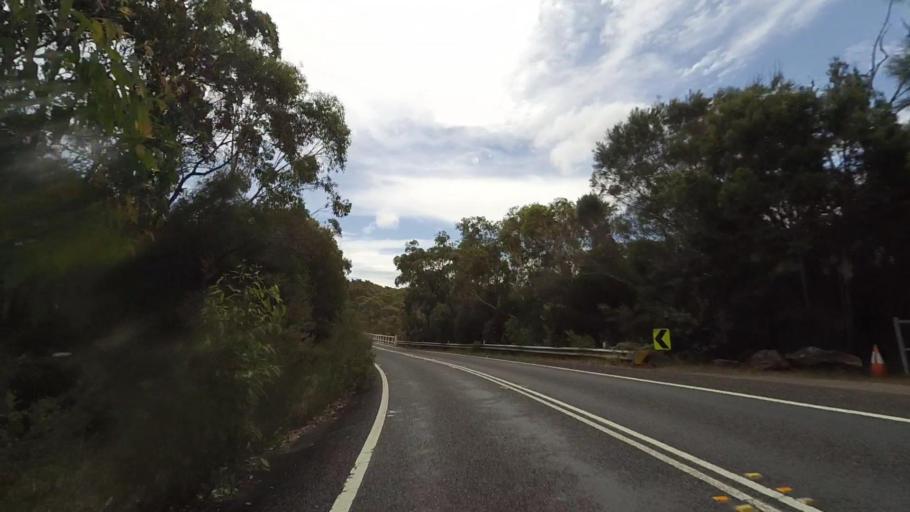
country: AU
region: New South Wales
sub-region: Sutherland Shire
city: Grays Point
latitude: -34.1150
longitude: 151.0687
